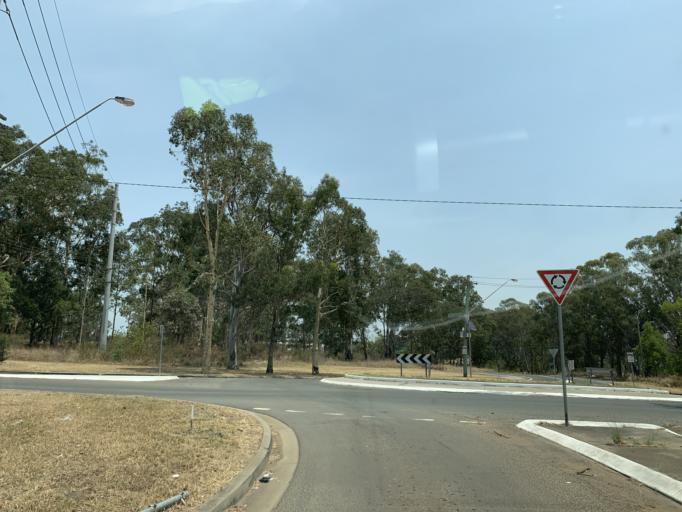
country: AU
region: New South Wales
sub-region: Fairfield
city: Horsley Park
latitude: -33.8343
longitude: 150.8738
